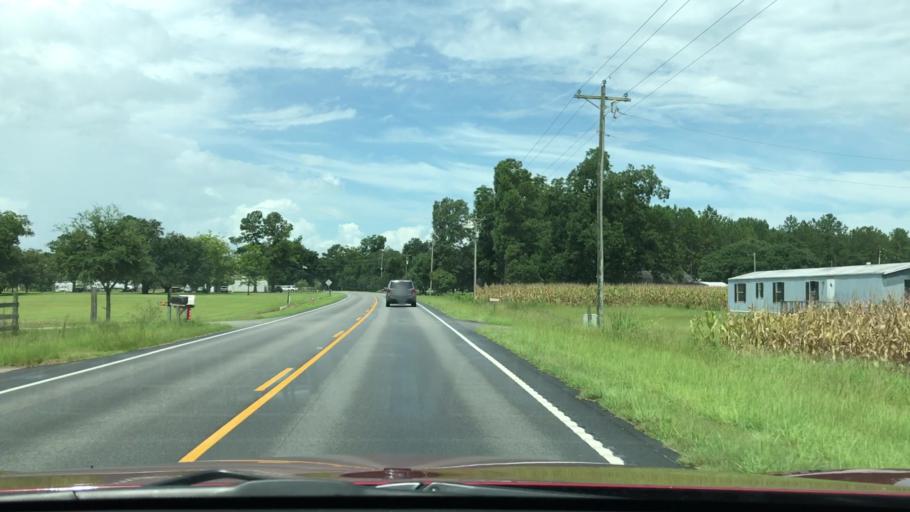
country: US
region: South Carolina
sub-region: Horry County
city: Loris
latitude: 33.9016
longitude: -78.8828
